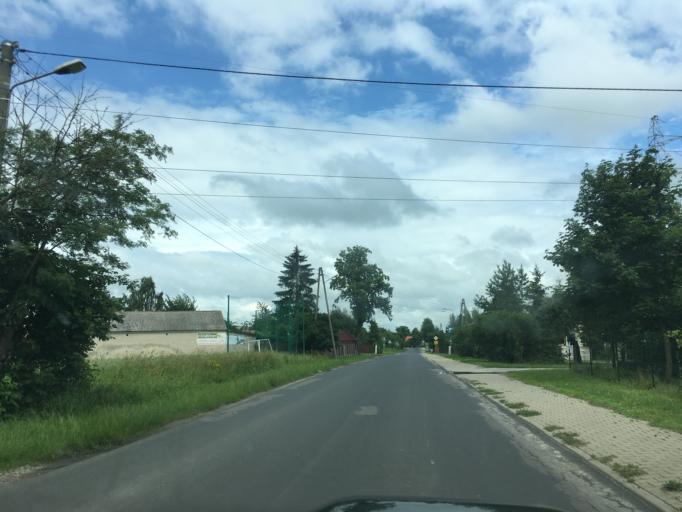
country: PL
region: Lublin Voivodeship
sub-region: Powiat swidnicki
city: Swidnik
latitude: 51.2048
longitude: 22.7358
